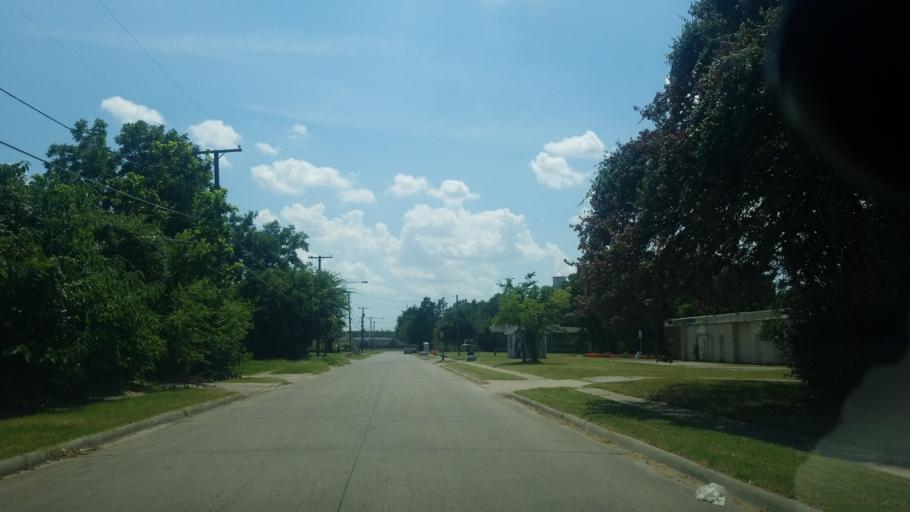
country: US
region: Texas
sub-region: Dallas County
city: Hutchins
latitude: 32.7153
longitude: -96.7471
